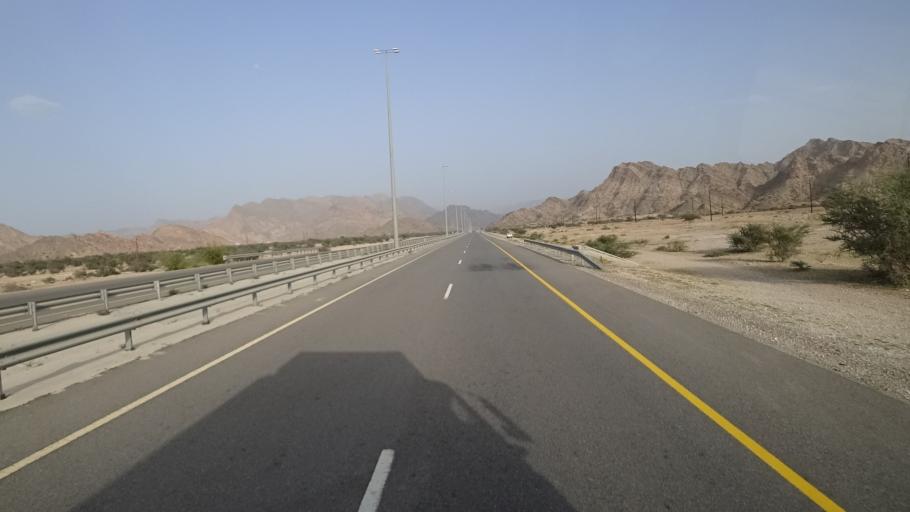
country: OM
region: Muhafazat Masqat
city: Muscat
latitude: 23.3680
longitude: 58.6456
